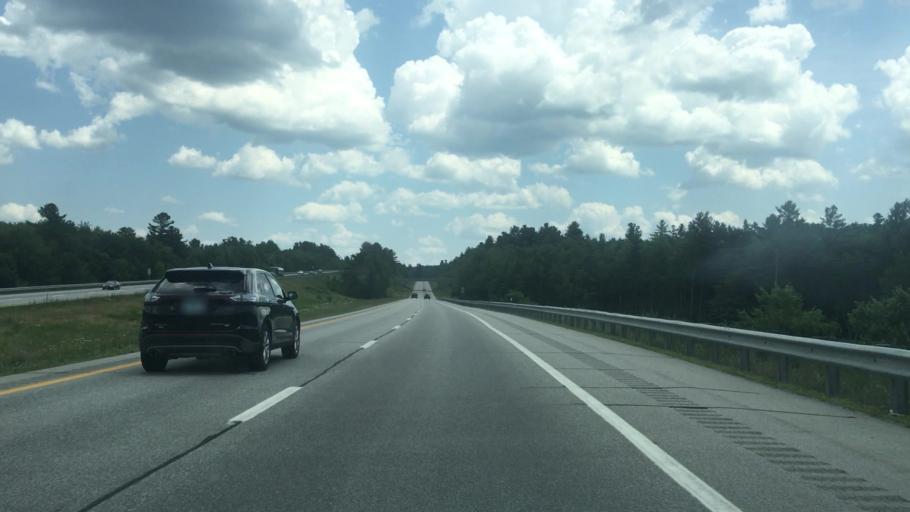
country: US
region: New Hampshire
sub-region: Merrimack County
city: New London
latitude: 43.4052
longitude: -72.0222
